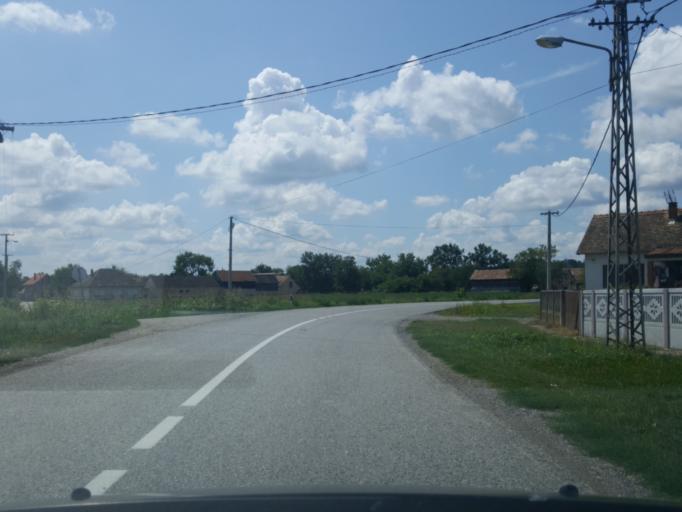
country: RS
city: Metkovic
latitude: 44.8517
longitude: 19.5342
